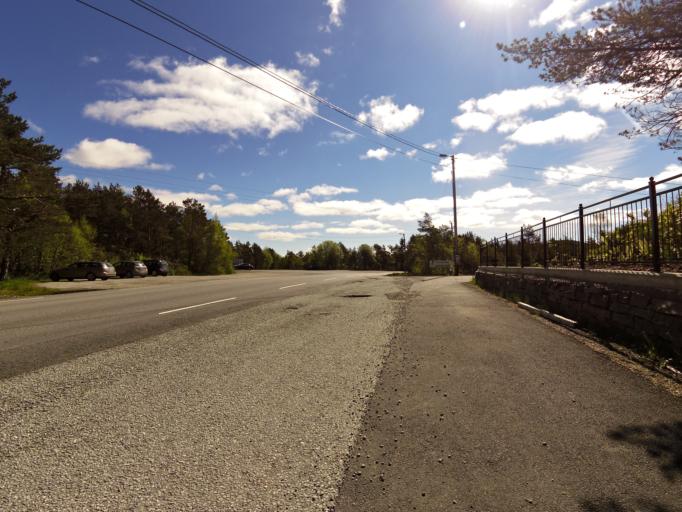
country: NO
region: Hordaland
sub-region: Os
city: Hagavik
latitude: 60.2570
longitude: 5.3625
